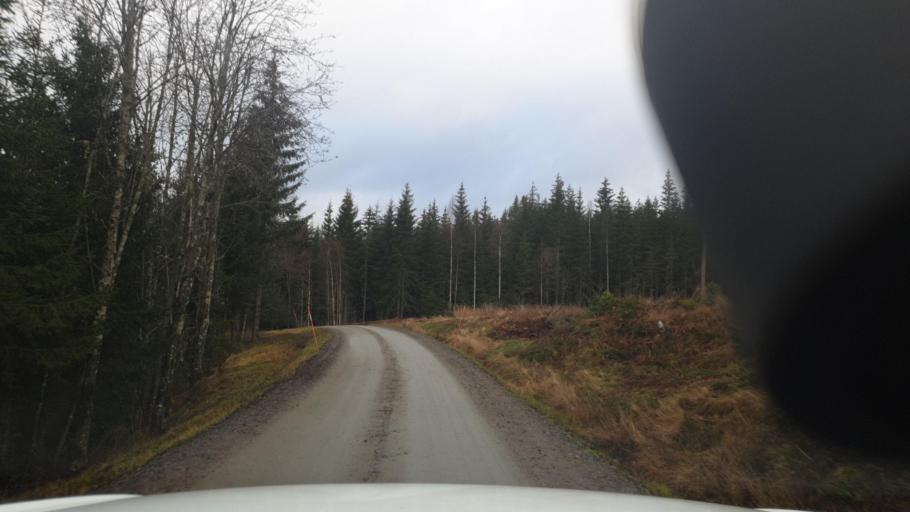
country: SE
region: Vaermland
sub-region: Sunne Kommun
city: Sunne
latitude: 59.6654
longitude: 13.0406
